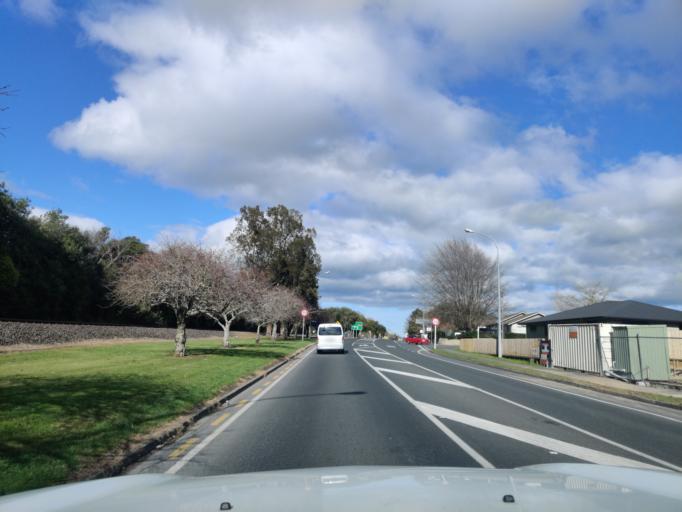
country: NZ
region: Waikato
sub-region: Matamata-Piako District
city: Matamata
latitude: -37.8225
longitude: 175.7710
